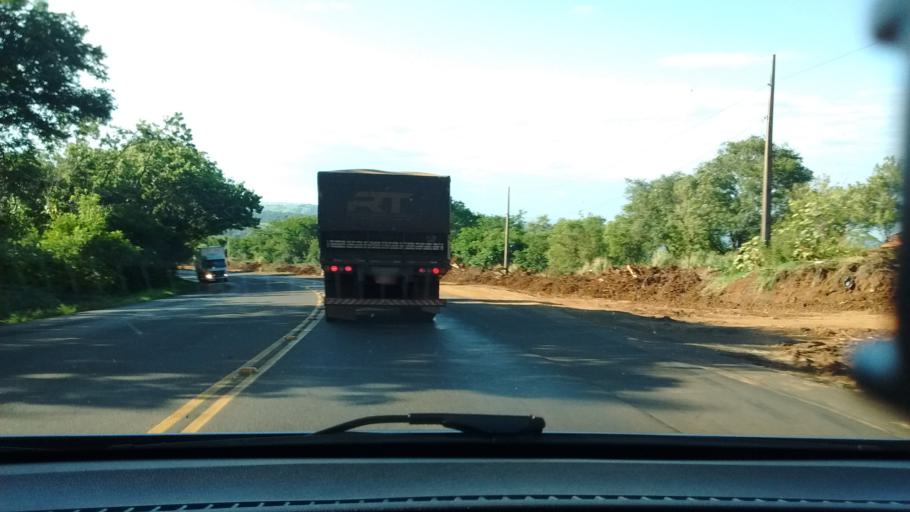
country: BR
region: Parana
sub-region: Cascavel
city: Cascavel
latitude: -25.1980
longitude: -53.6030
